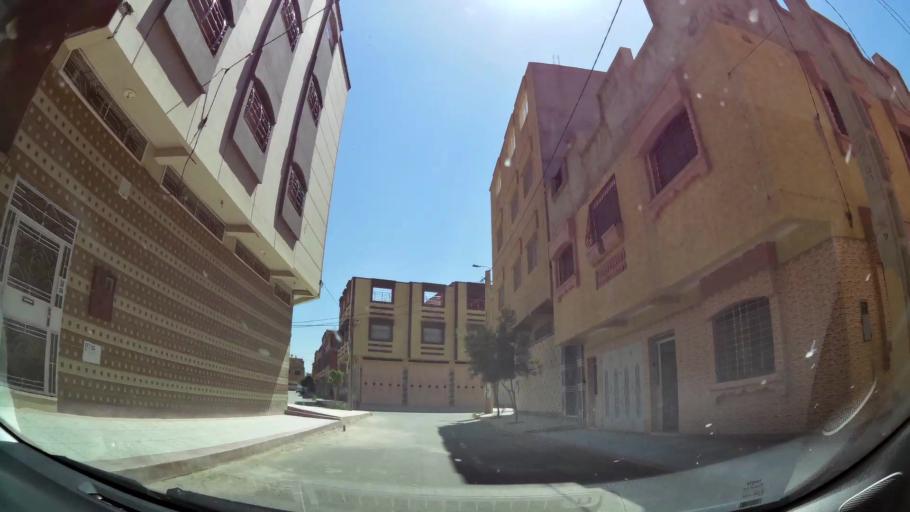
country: MA
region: Oriental
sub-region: Oujda-Angad
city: Oujda
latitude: 34.6887
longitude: -1.9405
